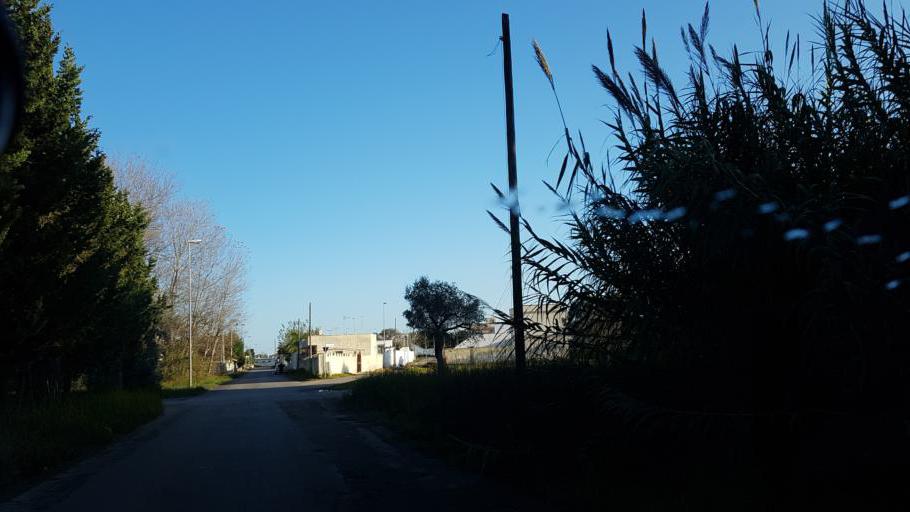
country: IT
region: Apulia
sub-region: Provincia di Brindisi
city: Torchiarolo
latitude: 40.5023
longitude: 18.1117
